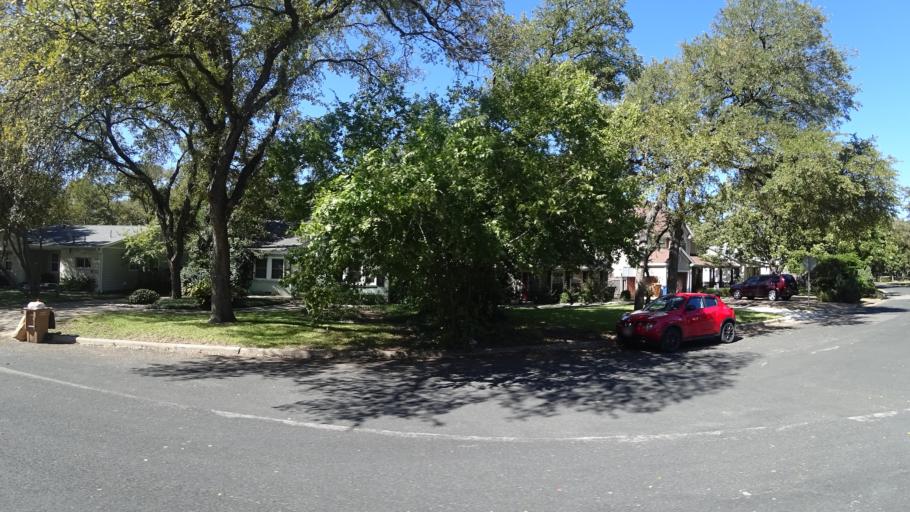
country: US
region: Texas
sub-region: Travis County
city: Austin
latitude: 30.2955
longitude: -97.7599
